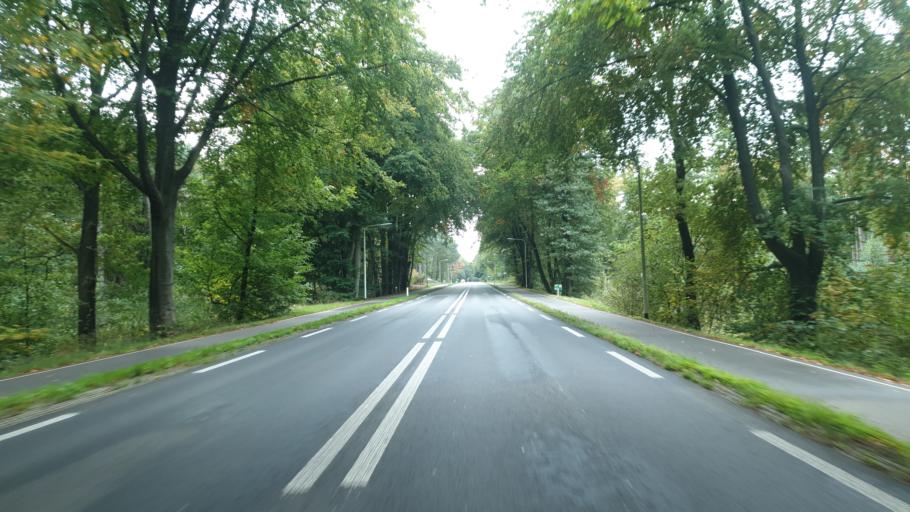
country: NL
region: Gelderland
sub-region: Gemeente Groesbeek
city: Berg en Dal
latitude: 51.7999
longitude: 5.9024
